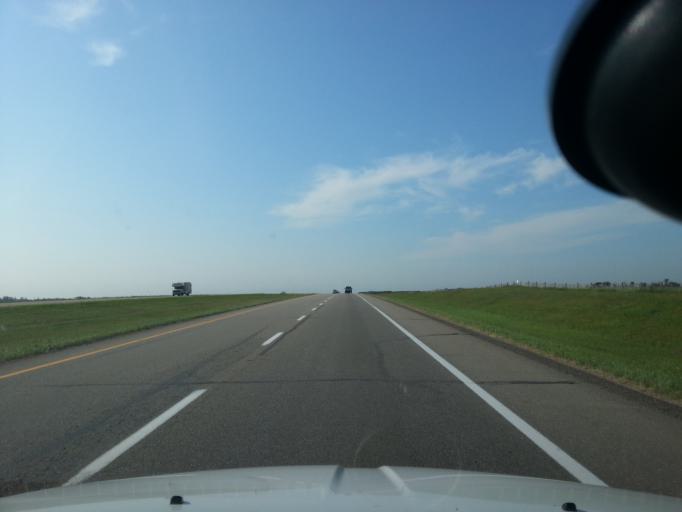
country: CA
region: Alberta
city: Ponoka
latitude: 52.7397
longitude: -113.6441
